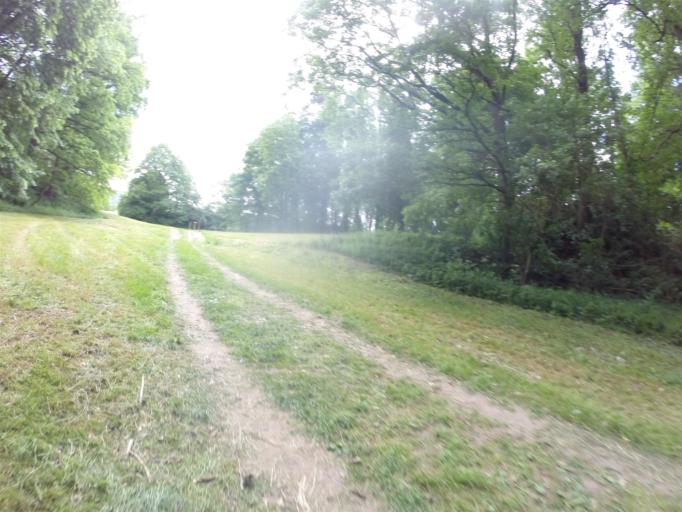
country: DE
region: Thuringia
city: Laasdorf
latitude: 50.8787
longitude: 11.6567
